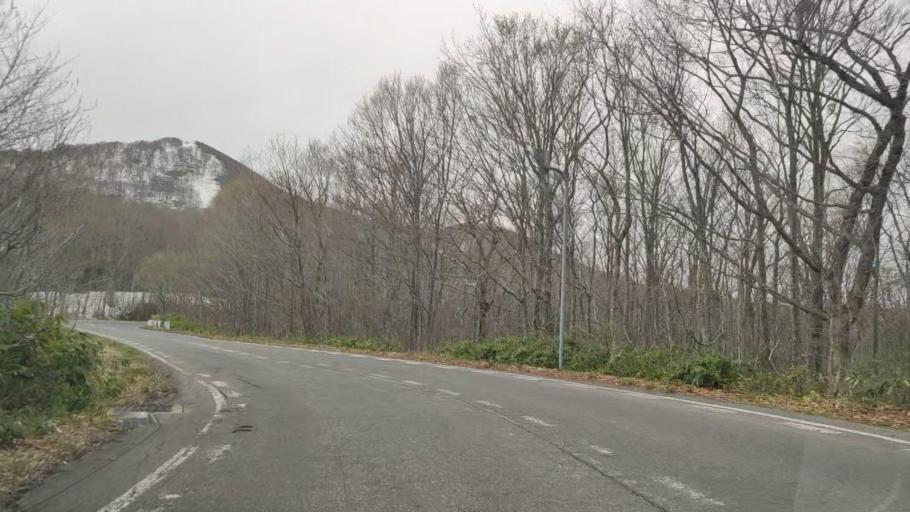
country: JP
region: Aomori
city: Aomori Shi
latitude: 40.6575
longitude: 140.9555
